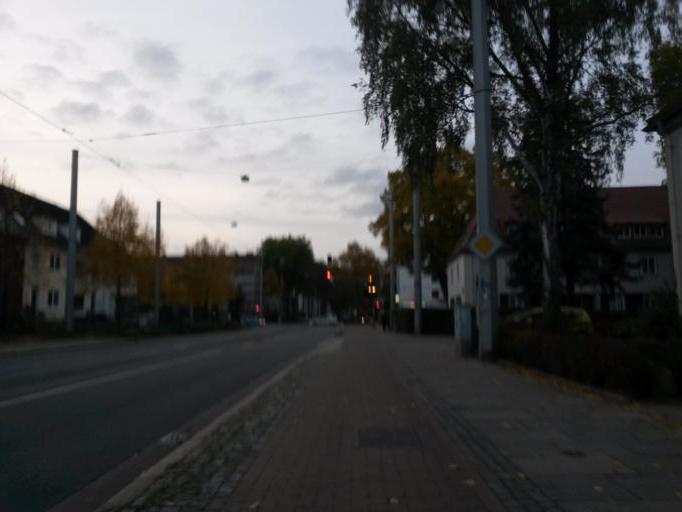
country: DE
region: Bremen
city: Bremen
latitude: 53.0669
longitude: 8.8557
